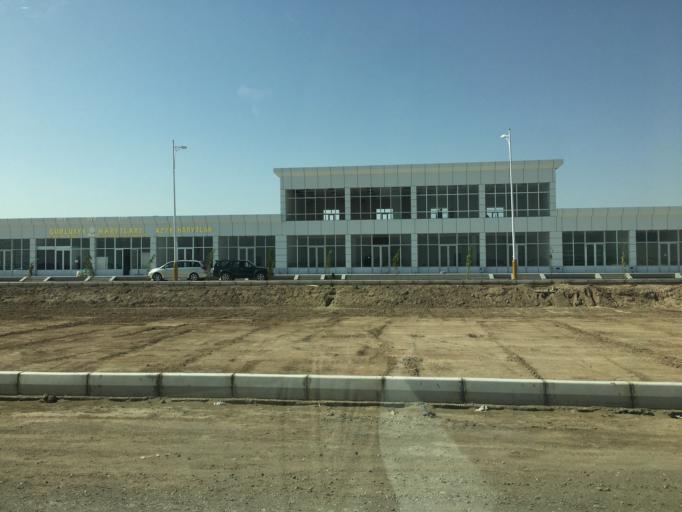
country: TM
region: Lebap
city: Turkmenabat
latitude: 39.0111
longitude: 63.6043
